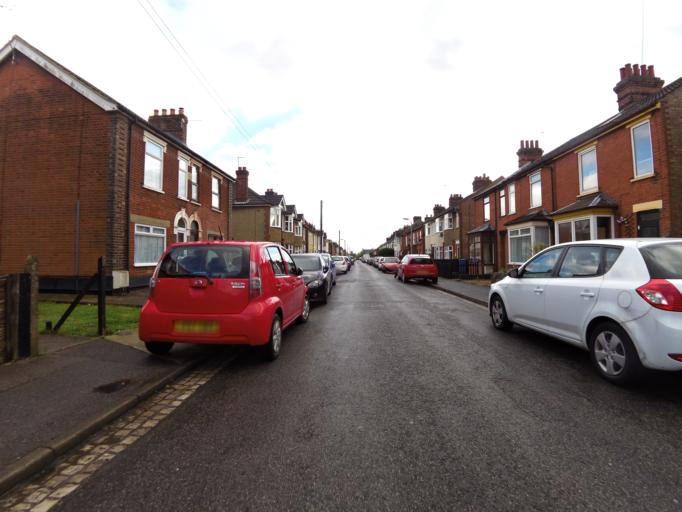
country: GB
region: England
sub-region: Suffolk
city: Ipswich
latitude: 52.0508
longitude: 1.1902
